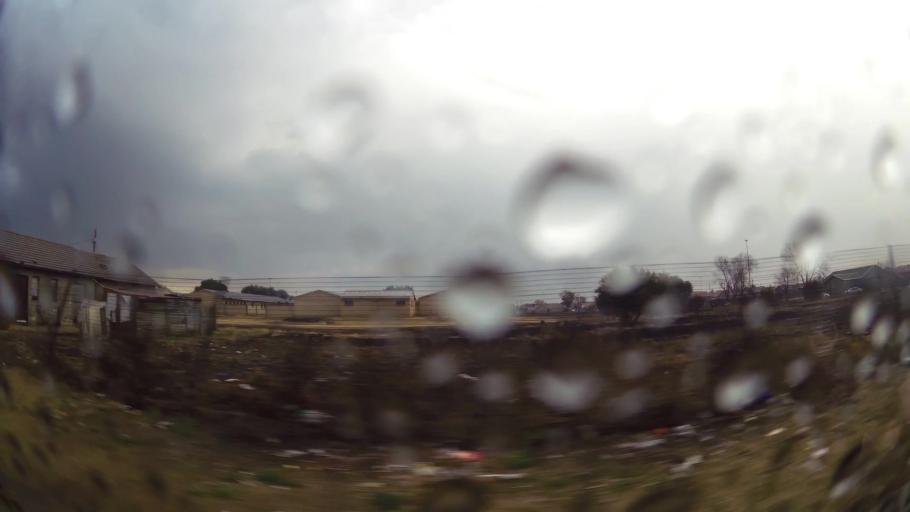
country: ZA
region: Gauteng
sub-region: Ekurhuleni Metropolitan Municipality
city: Germiston
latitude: -26.3613
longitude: 28.1301
